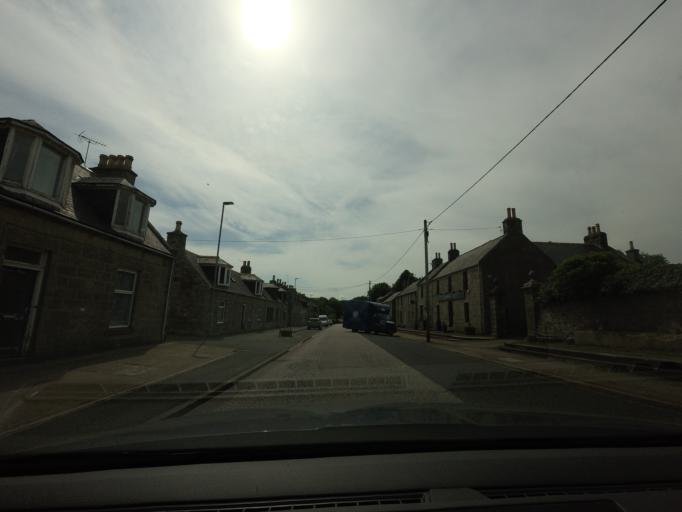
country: GB
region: Scotland
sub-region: Aberdeenshire
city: Rosehearty
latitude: 57.5948
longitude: -2.1990
